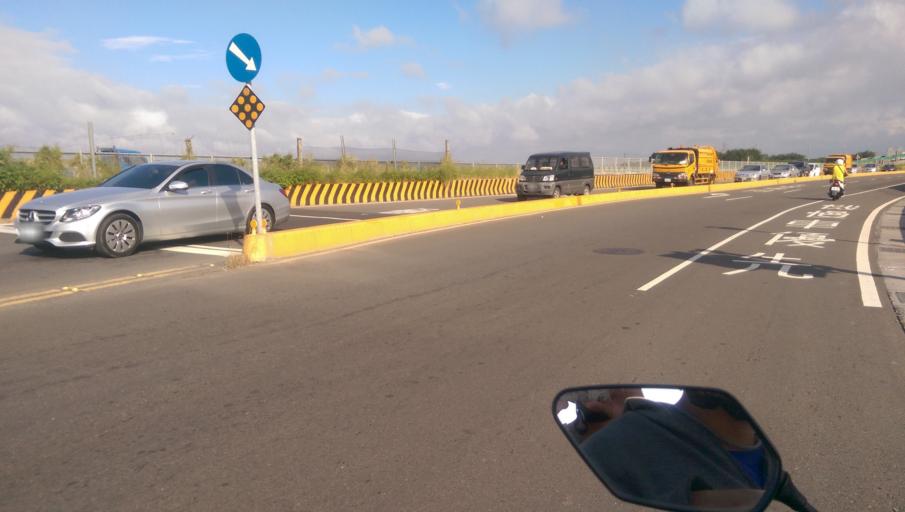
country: TW
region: Taiwan
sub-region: Hsinchu
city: Hsinchu
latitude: 24.8324
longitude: 120.9535
